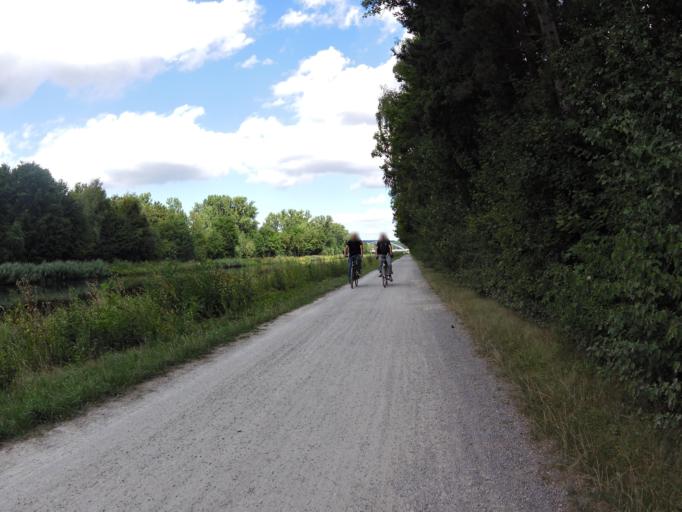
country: DE
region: Bavaria
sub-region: Regierungsbezirk Unterfranken
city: Volkach
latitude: 49.8555
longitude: 10.2250
